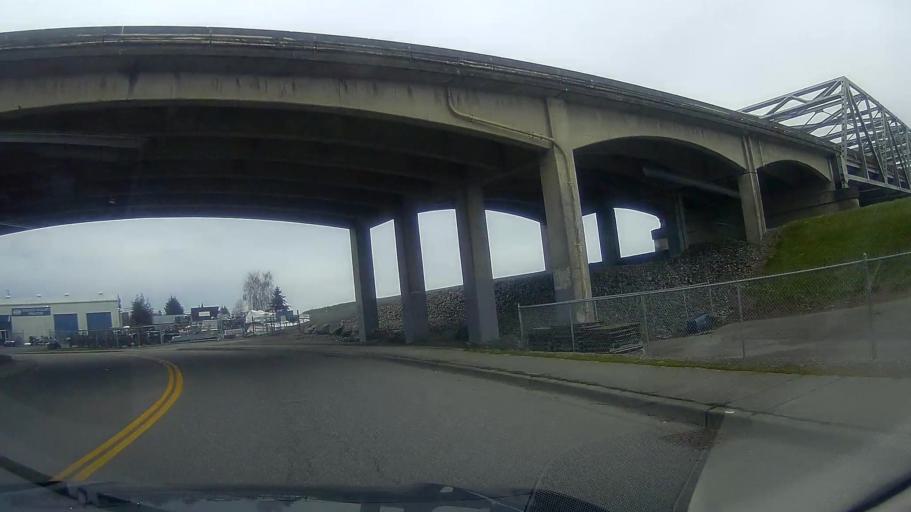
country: US
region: Washington
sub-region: Skagit County
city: Mount Vernon
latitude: 48.4435
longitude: -122.3396
